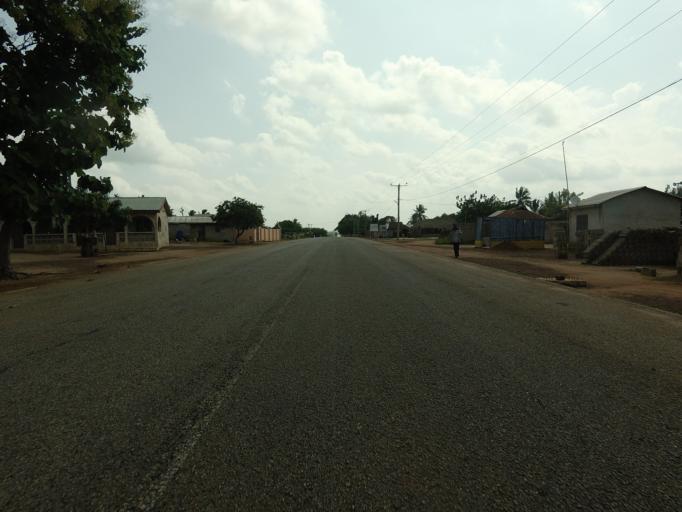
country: TG
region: Maritime
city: Tsevie
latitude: 6.3921
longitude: 0.8346
